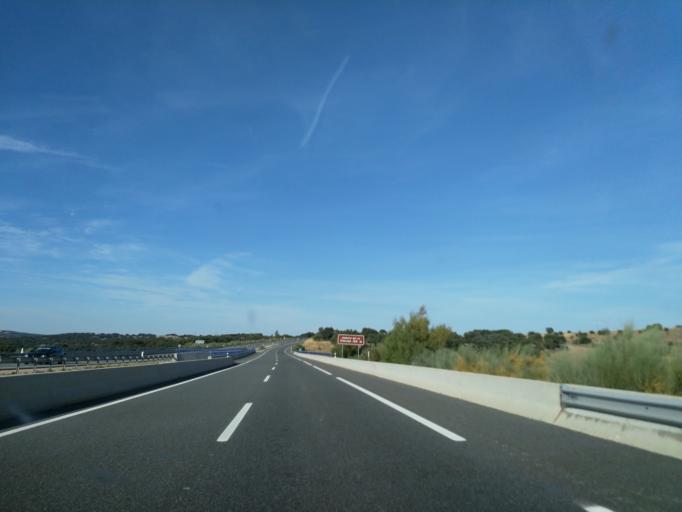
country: ES
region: Castille and Leon
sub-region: Provincia de Avila
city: Mediana de Voltoya
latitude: 40.7062
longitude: -4.5634
